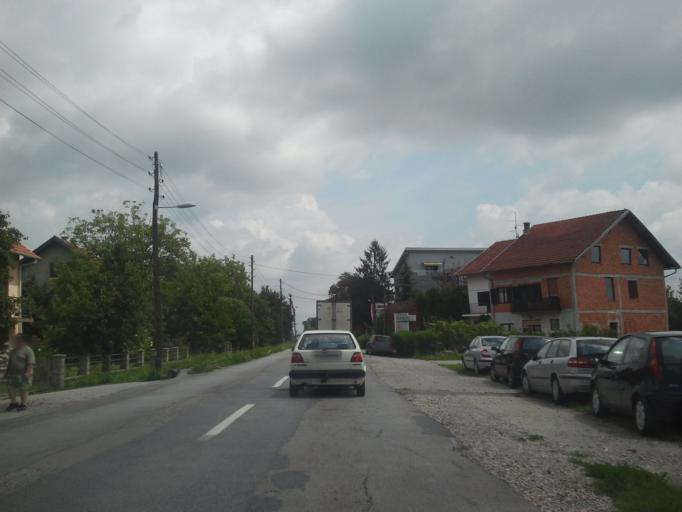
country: HR
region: Grad Zagreb
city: Lucko
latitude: 45.7561
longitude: 15.8435
